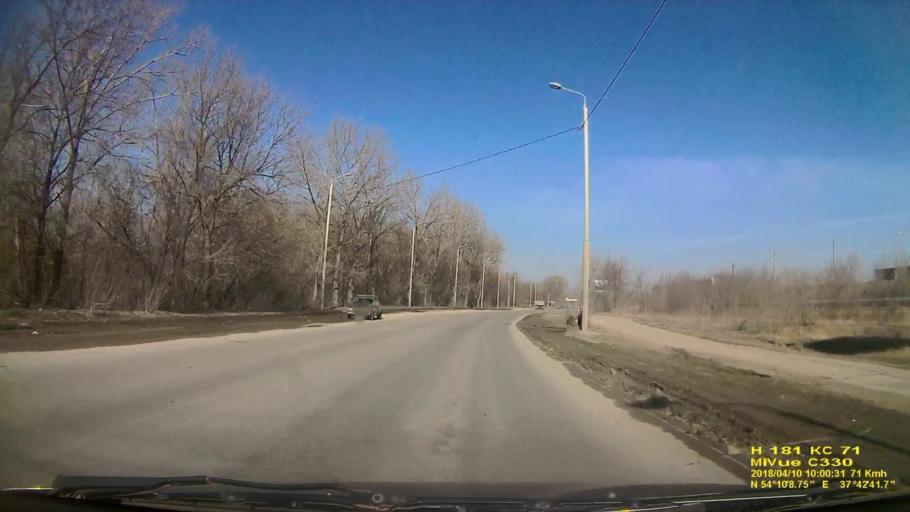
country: RU
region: Tula
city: Tula
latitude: 54.1692
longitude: 37.7114
